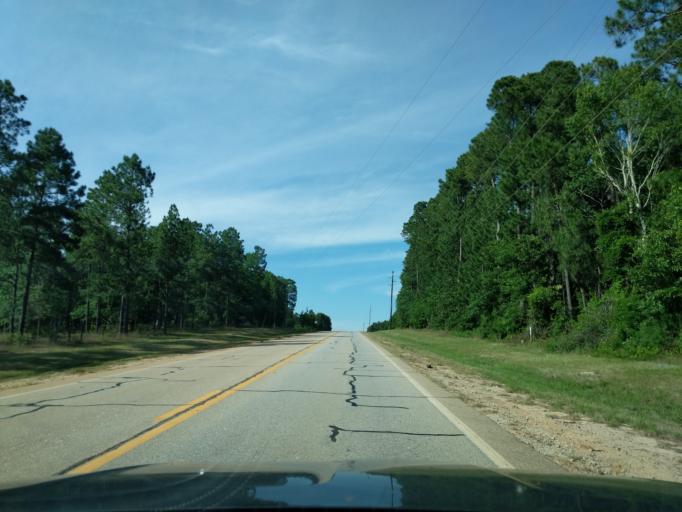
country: US
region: Georgia
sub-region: Jefferson County
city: Wrens
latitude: 33.2849
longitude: -82.3829
